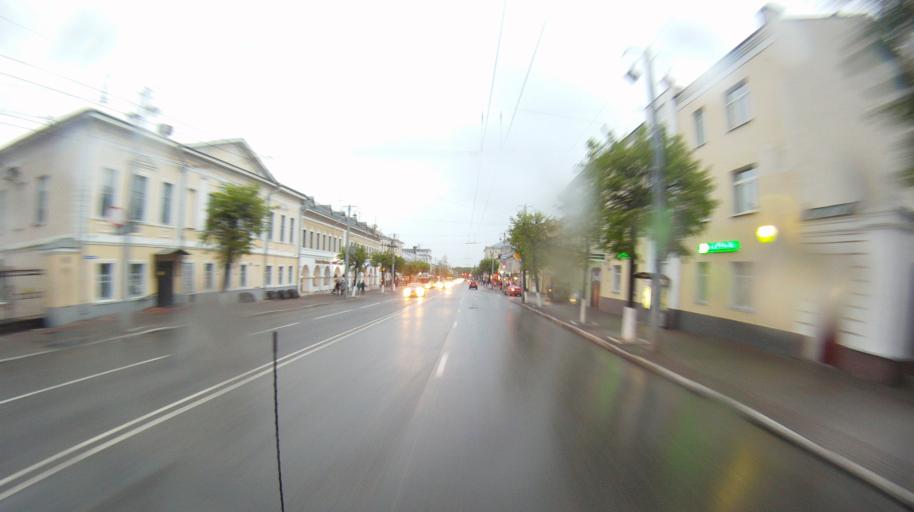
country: RU
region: Vladimir
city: Vladimir
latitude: 56.1269
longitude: 40.3979
